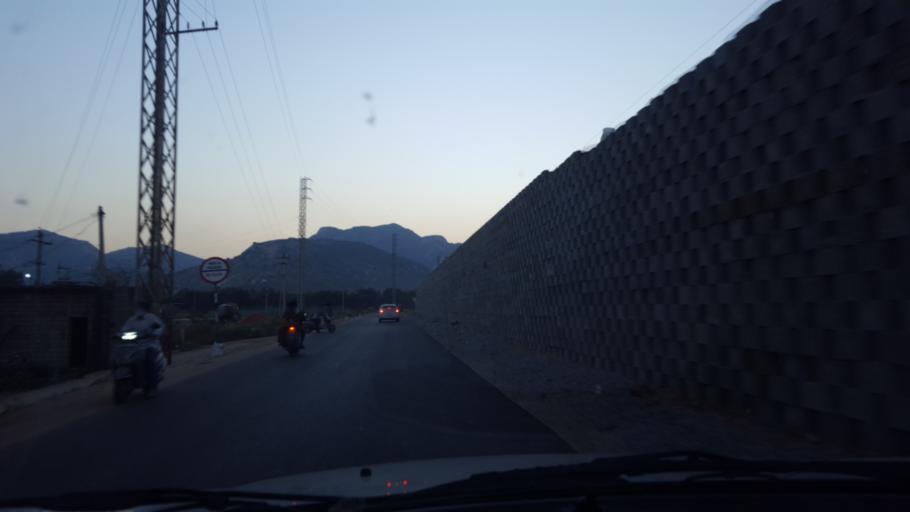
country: IN
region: Andhra Pradesh
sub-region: Chittoor
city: Narasingapuram
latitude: 13.5798
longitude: 79.3159
